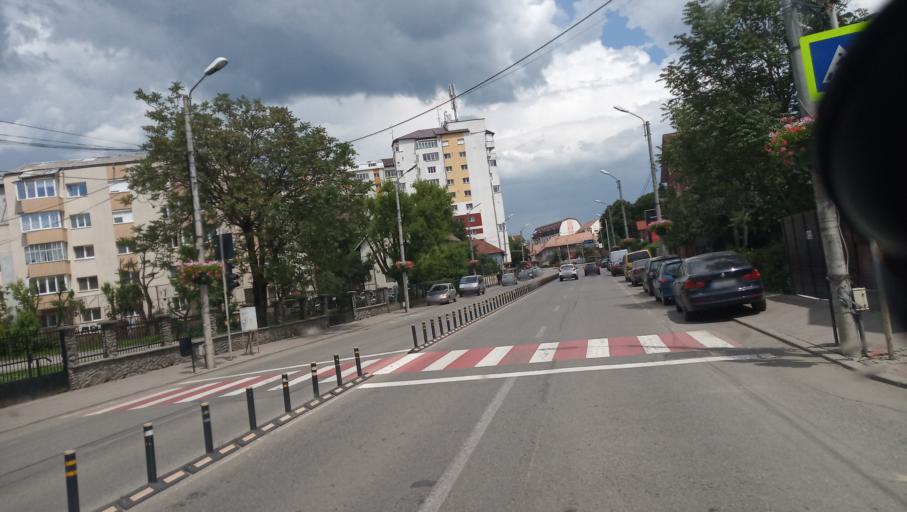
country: RO
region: Bistrita-Nasaud
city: Bistrita
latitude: 47.1401
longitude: 24.5038
